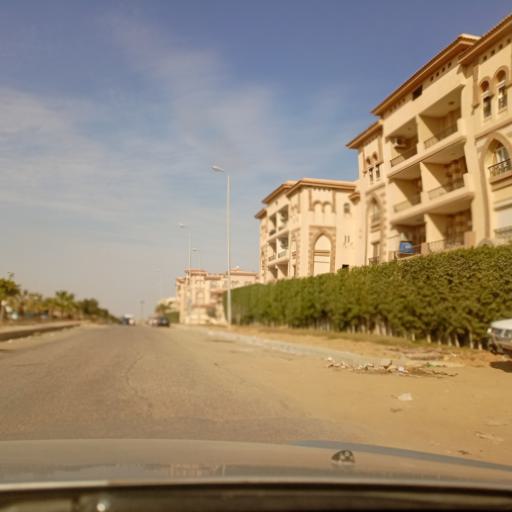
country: EG
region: Muhafazat al Qalyubiyah
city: Al Khankah
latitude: 30.0471
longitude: 31.4852
